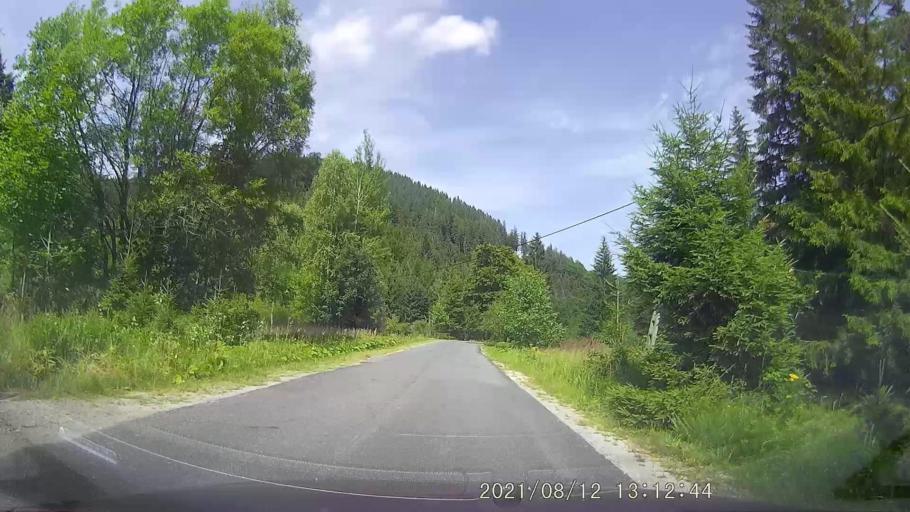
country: PL
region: Lower Silesian Voivodeship
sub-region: Powiat klodzki
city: Stronie Slaskie
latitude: 50.2490
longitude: 16.8512
